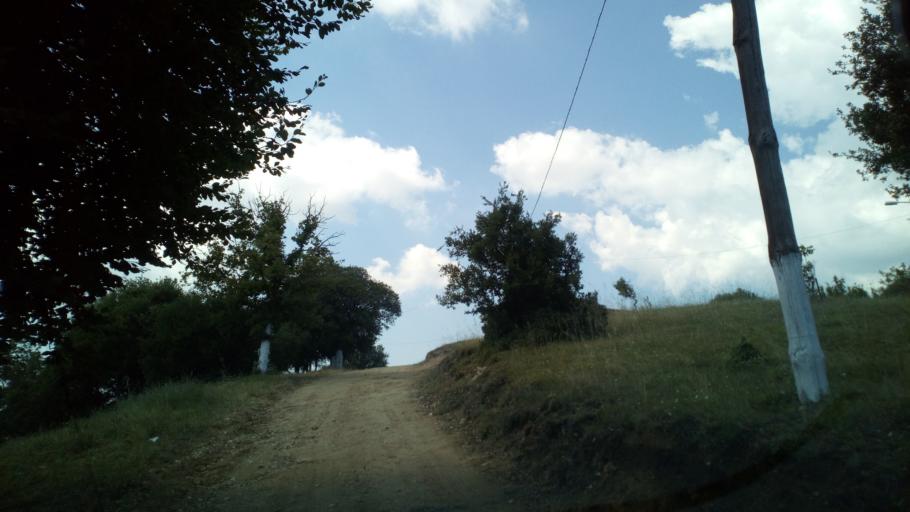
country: GR
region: Central Macedonia
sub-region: Nomos Thessalonikis
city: Sochos
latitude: 40.8252
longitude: 23.3439
